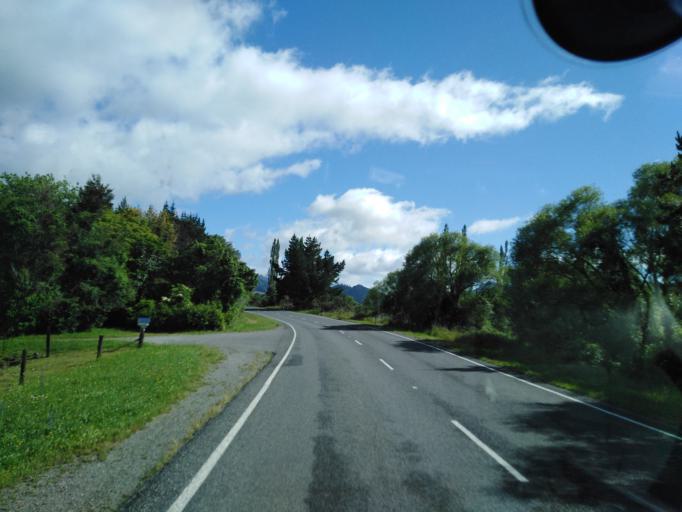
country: NZ
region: Nelson
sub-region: Nelson City
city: Nelson
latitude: -41.2490
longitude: 173.5778
